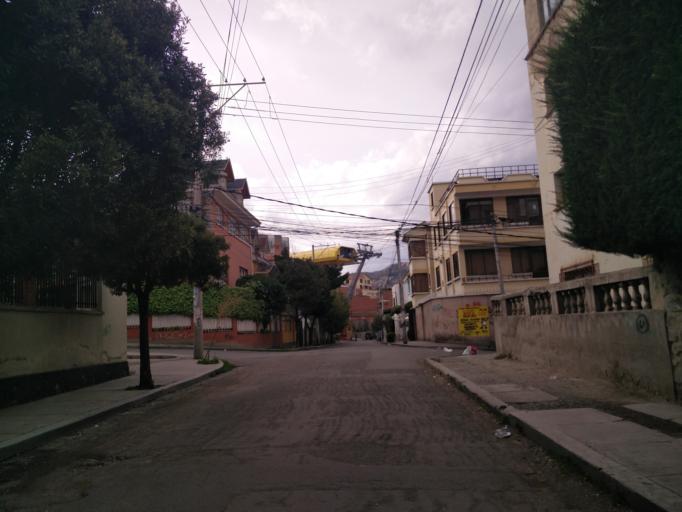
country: BO
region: La Paz
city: La Paz
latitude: -16.5158
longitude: -68.1298
